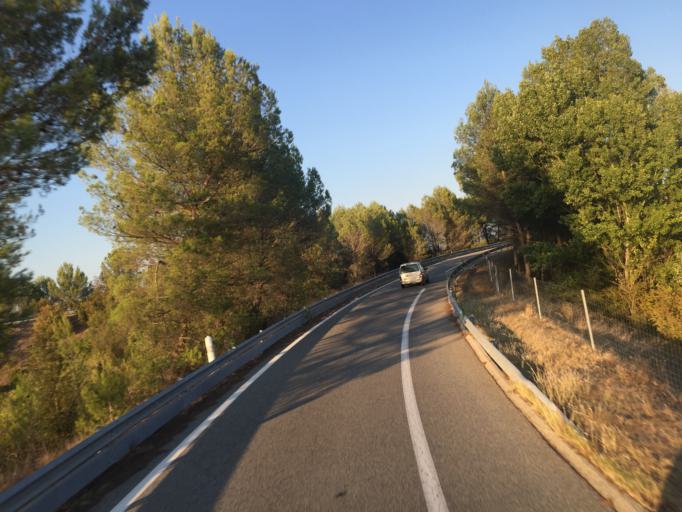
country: FR
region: Provence-Alpes-Cote d'Azur
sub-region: Departement du Vaucluse
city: Beaumont-de-Pertuis
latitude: 43.7036
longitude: 5.7299
